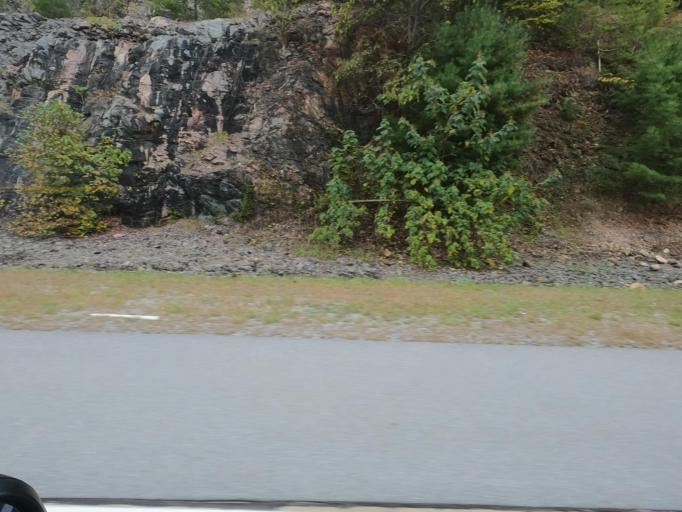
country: US
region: Tennessee
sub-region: Unicoi County
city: Banner Hill
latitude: 36.0566
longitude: -82.5129
